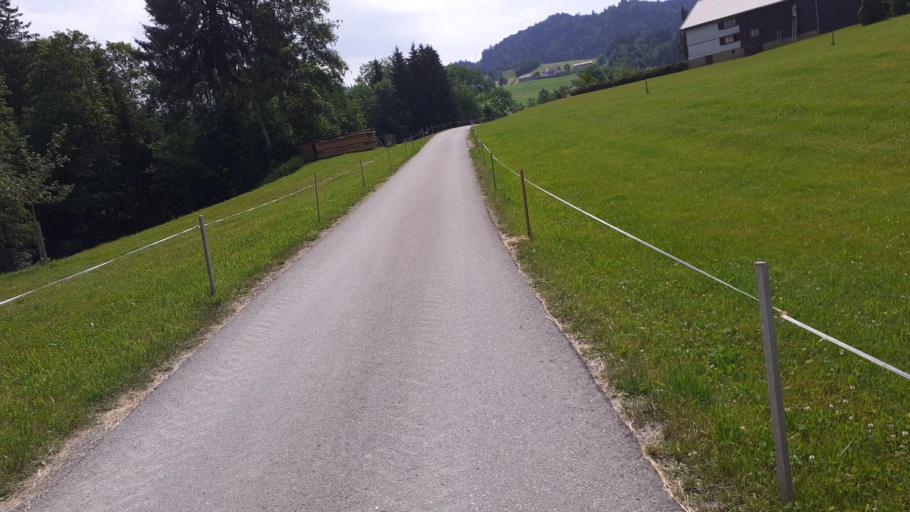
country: AT
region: Vorarlberg
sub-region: Politischer Bezirk Bregenz
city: Bildstein
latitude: 47.4482
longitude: 9.8152
